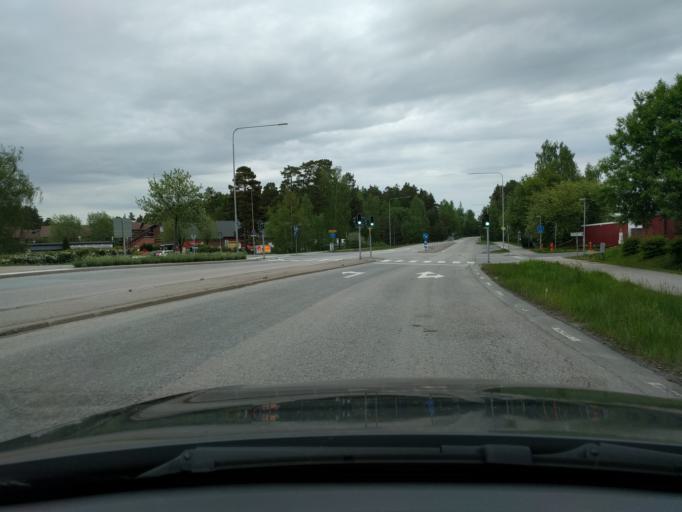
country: SE
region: Stockholm
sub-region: Taby Kommun
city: Taby
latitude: 59.4646
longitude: 18.0437
